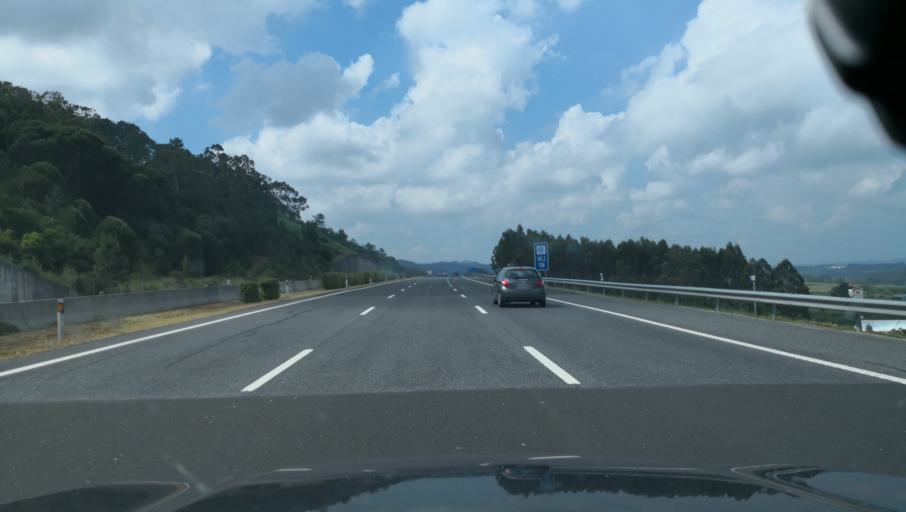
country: PT
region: Leiria
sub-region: Caldas da Rainha
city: Caldas da Rainha
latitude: 39.4908
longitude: -9.0947
